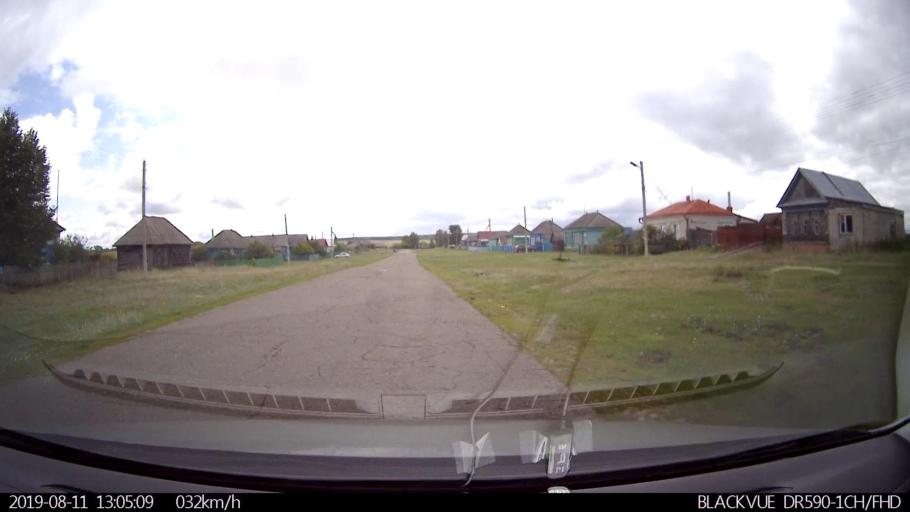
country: RU
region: Ulyanovsk
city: Ignatovka
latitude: 53.8721
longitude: 47.6491
